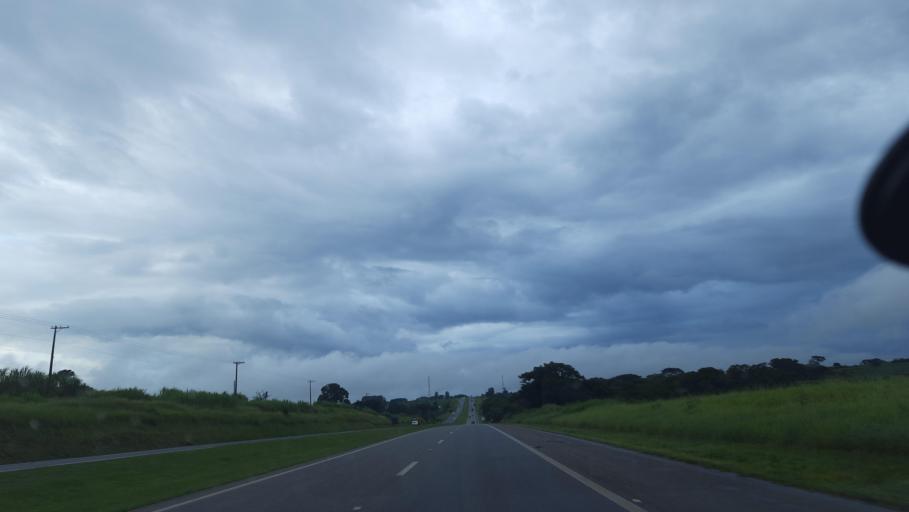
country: BR
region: Sao Paulo
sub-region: Aguai
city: Aguai
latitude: -22.2048
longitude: -46.9832
